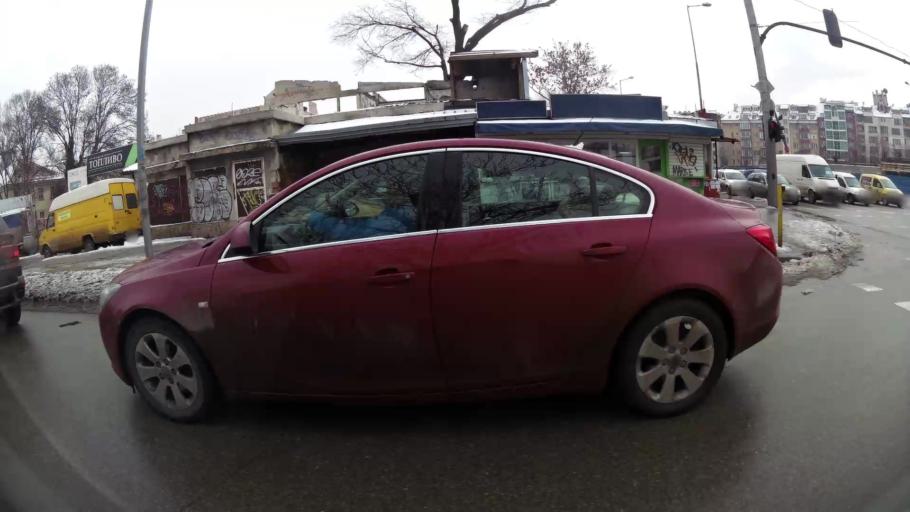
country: BG
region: Sofia-Capital
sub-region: Stolichna Obshtina
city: Sofia
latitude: 42.7051
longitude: 23.3337
